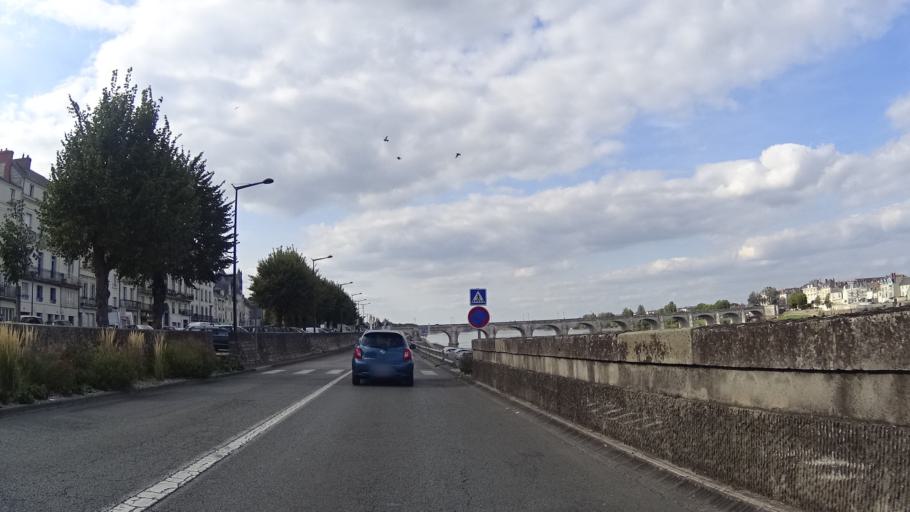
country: FR
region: Pays de la Loire
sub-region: Departement de Maine-et-Loire
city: Saumur
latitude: 47.2594
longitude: -0.0729
